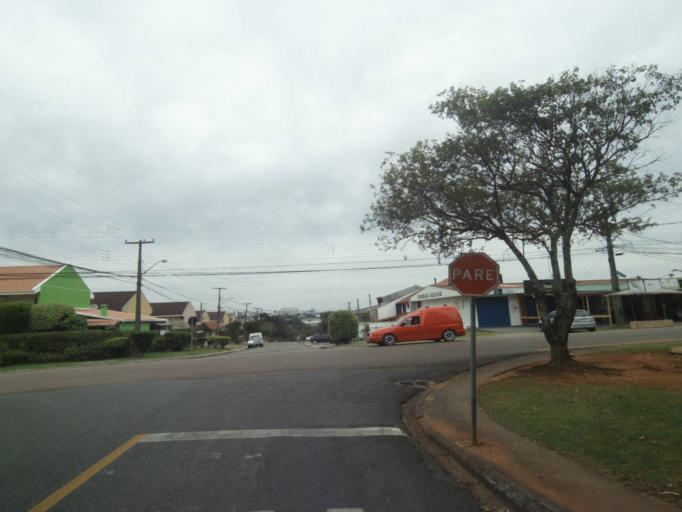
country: BR
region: Parana
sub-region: Pinhais
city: Pinhais
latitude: -25.4235
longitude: -49.2061
